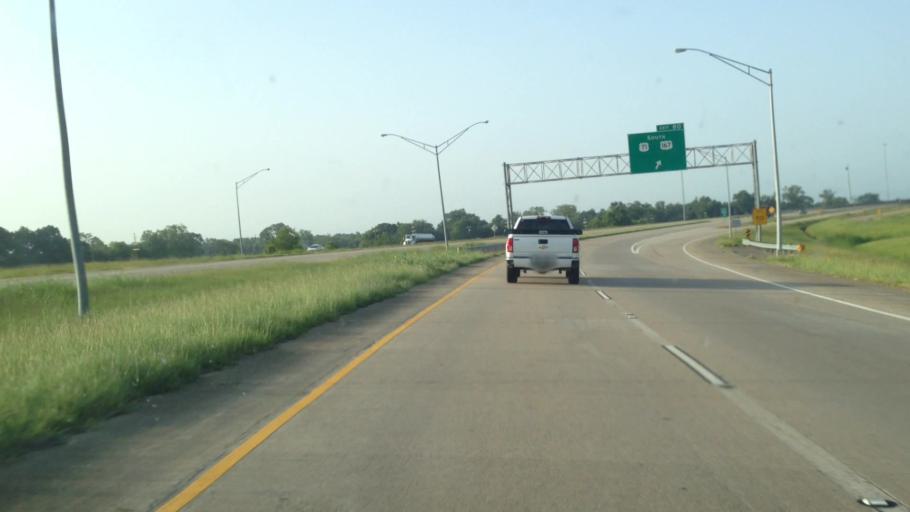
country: US
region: Louisiana
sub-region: Rapides Parish
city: Alexandria
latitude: 31.2486
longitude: -92.4293
